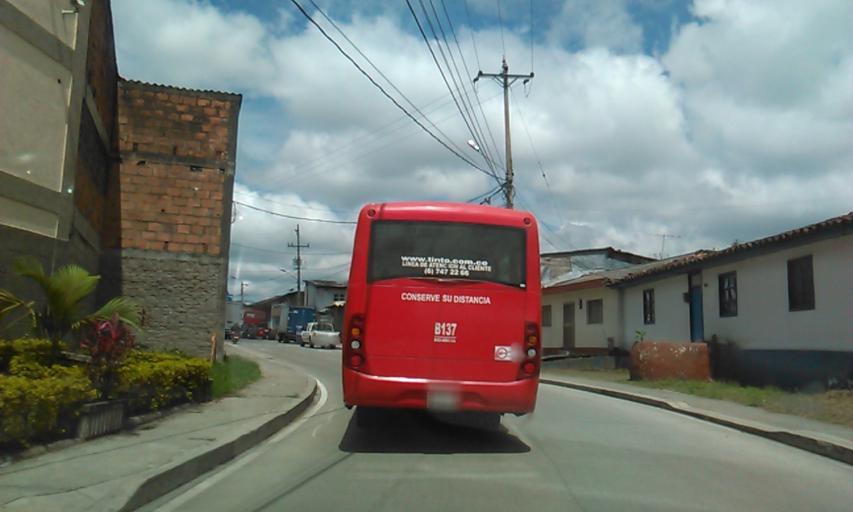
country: CO
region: Quindio
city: Armenia
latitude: 4.5138
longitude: -75.6875
